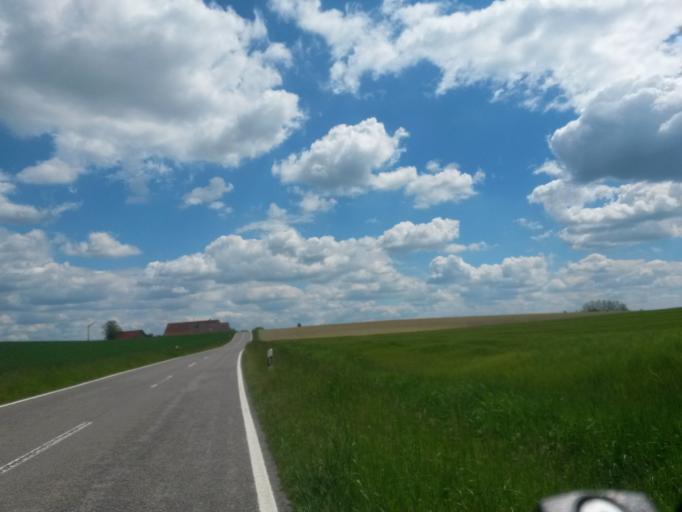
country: DE
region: Baden-Wuerttemberg
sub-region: Tuebingen Region
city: Bad Schussenried
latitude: 48.0019
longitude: 9.6962
